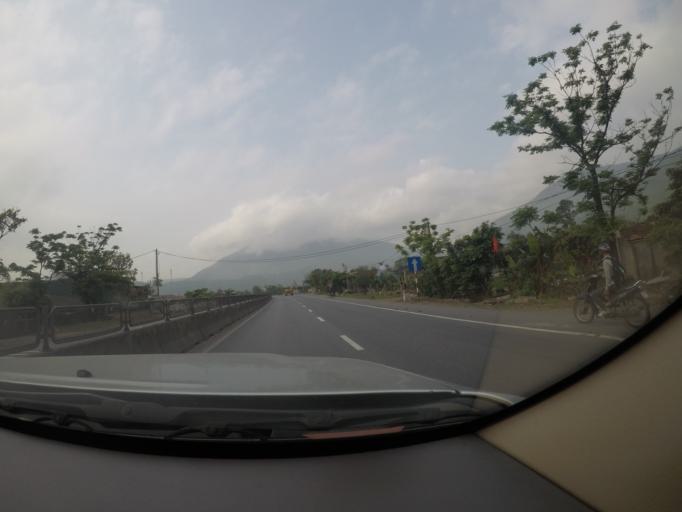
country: VN
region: Ha Tinh
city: Ky Anh
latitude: 17.9733
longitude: 106.4720
